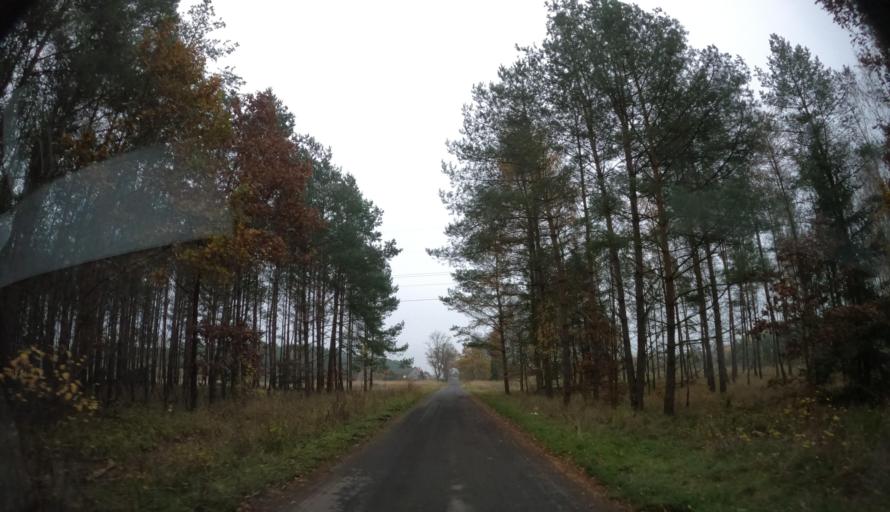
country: PL
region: West Pomeranian Voivodeship
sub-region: Powiat lobeski
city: Radowo Male
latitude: 53.6817
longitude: 15.4642
